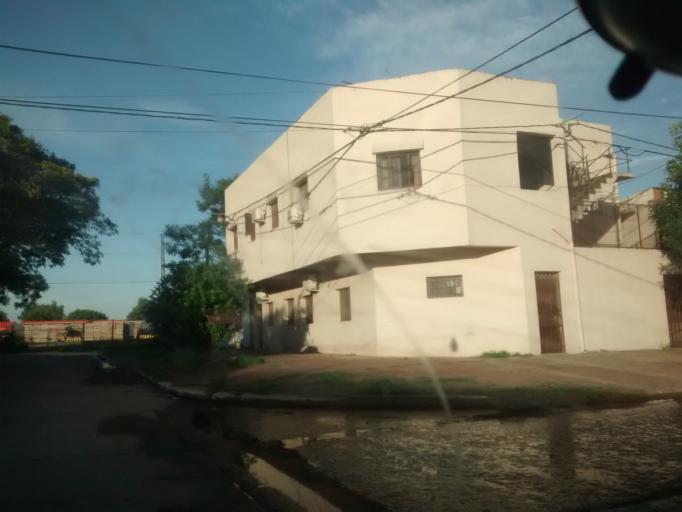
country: AR
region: Chaco
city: Resistencia
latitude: -27.4652
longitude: -58.9776
